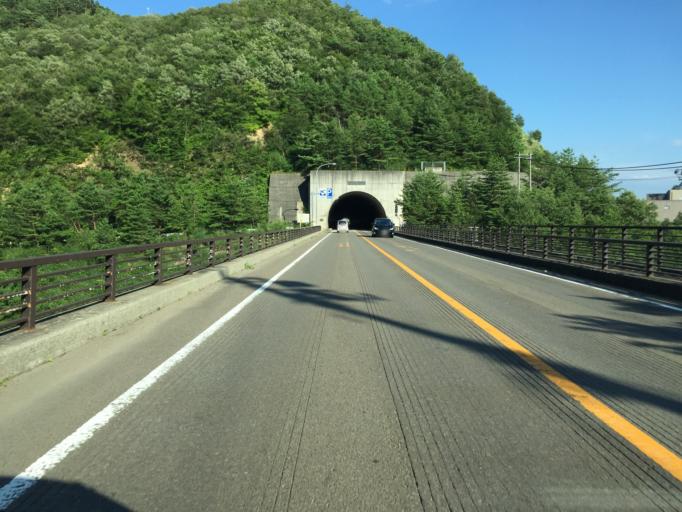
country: JP
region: Miyagi
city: Shiroishi
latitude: 37.9641
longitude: 140.5121
